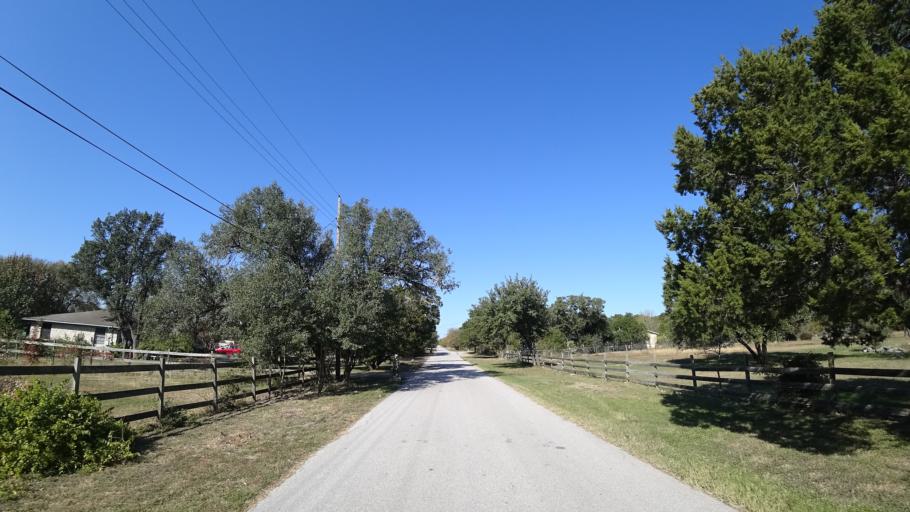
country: US
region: Texas
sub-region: Travis County
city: Barton Creek
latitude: 30.2272
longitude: -97.8546
